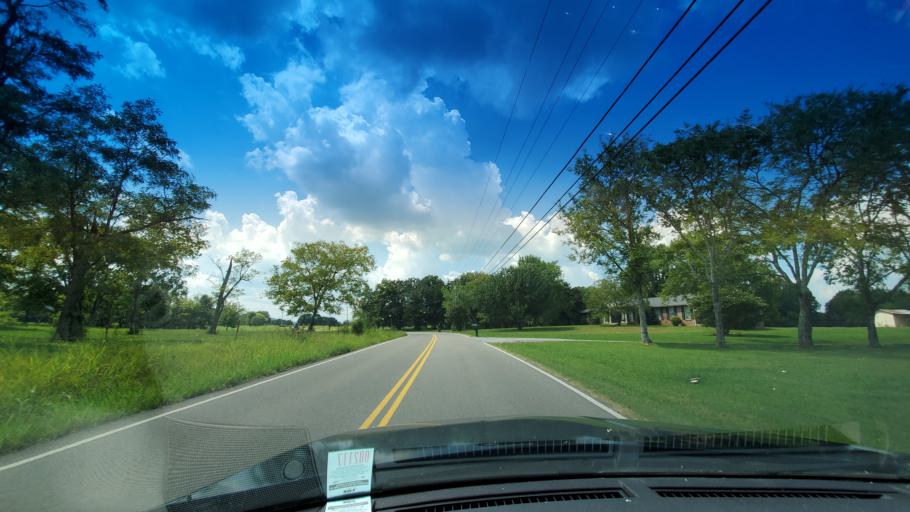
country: US
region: Tennessee
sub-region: Wilson County
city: Lebanon
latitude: 36.1801
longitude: -86.3323
